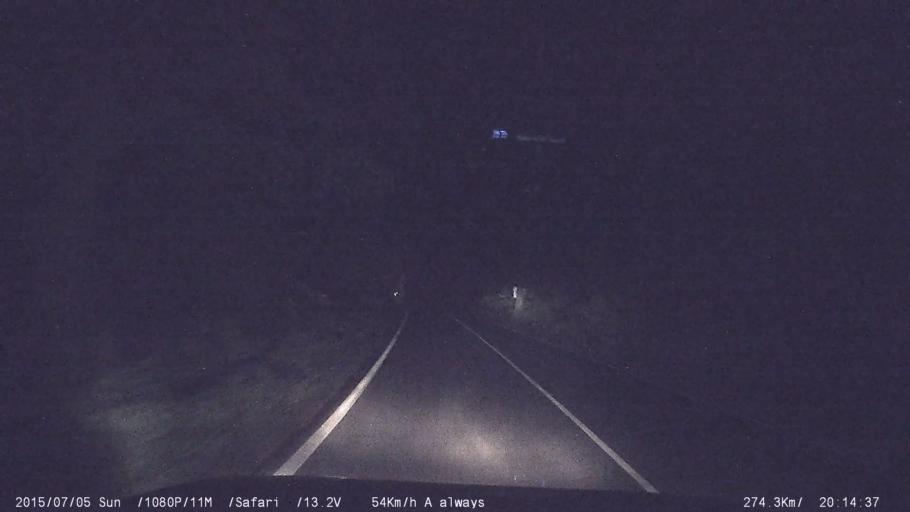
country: IN
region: Kerala
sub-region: Palakkad district
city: Palakkad
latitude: 10.8702
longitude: 76.5535
